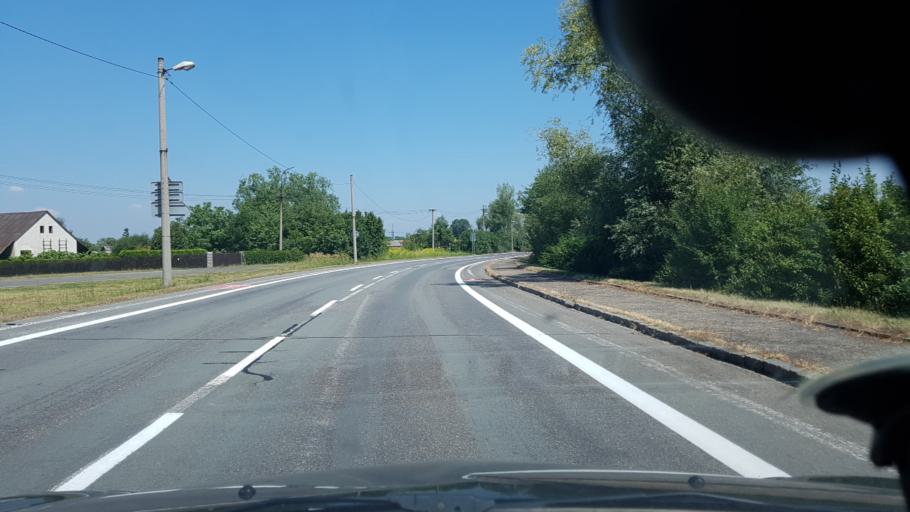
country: CZ
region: Moravskoslezsky
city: Stary Bohumin
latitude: 49.8971
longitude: 18.3330
